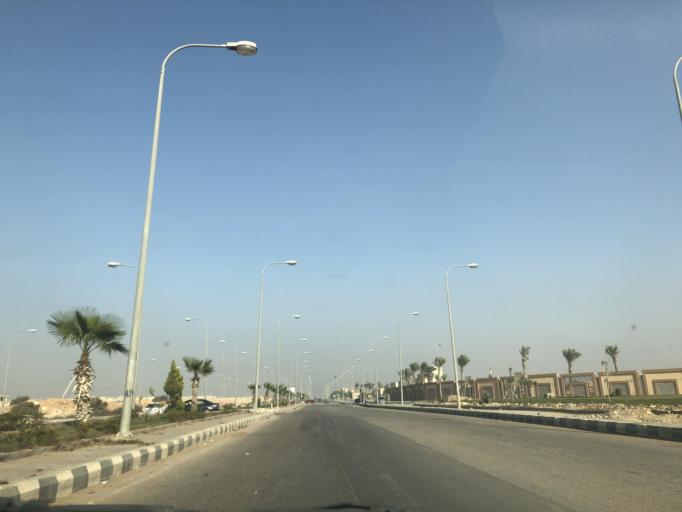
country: EG
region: Al Jizah
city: Madinat Sittah Uktubar
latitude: 29.9438
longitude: 31.0606
